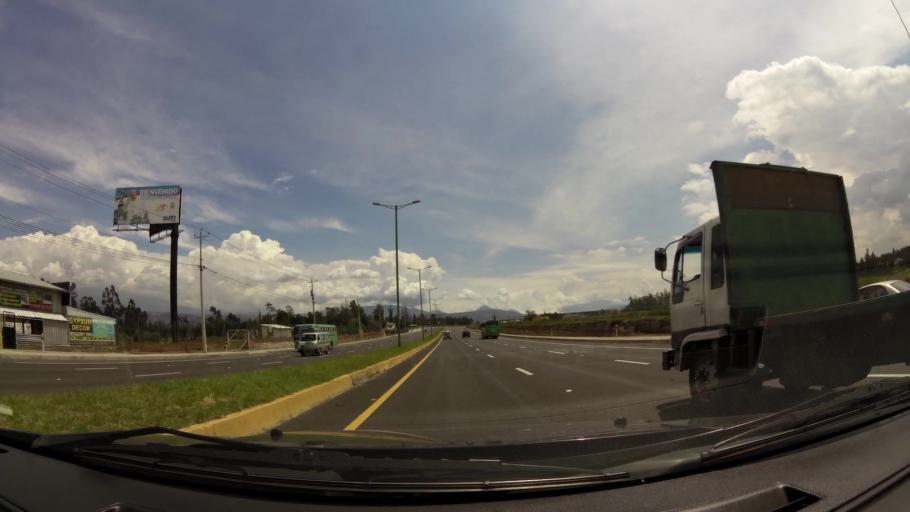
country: EC
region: Pichincha
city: Sangolqui
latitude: -0.1980
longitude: -78.3379
